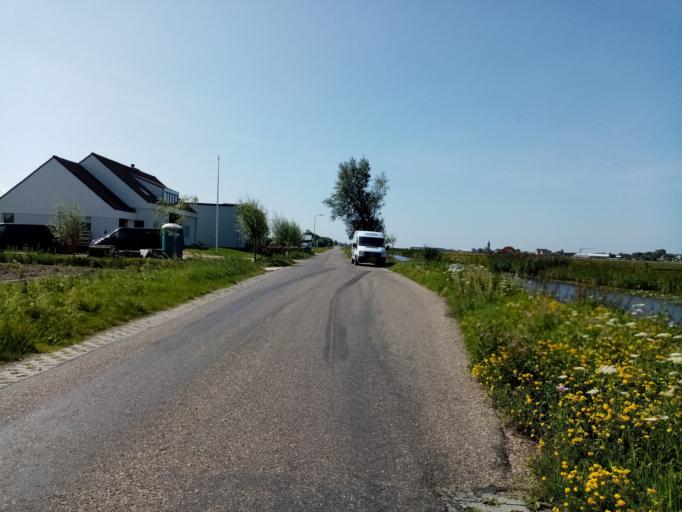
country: NL
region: South Holland
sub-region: Gemeente Hillegom
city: Hillegom
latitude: 52.3111
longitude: 4.5654
